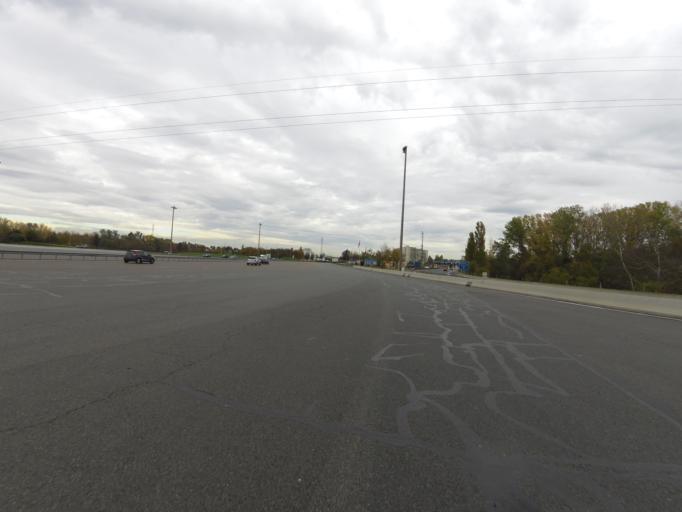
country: FR
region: Rhone-Alpes
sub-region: Departement du Rhone
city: Villefranche-sur-Saone
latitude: 45.9734
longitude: 4.7335
